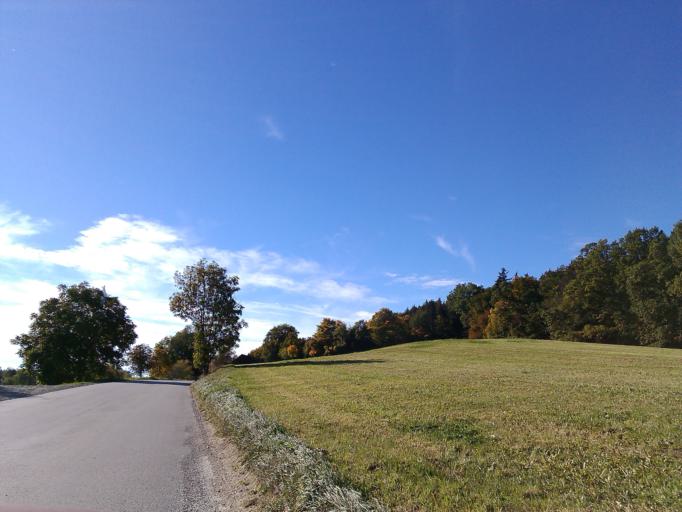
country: DE
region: Bavaria
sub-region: Upper Bavaria
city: Wessling
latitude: 48.0562
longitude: 11.2788
